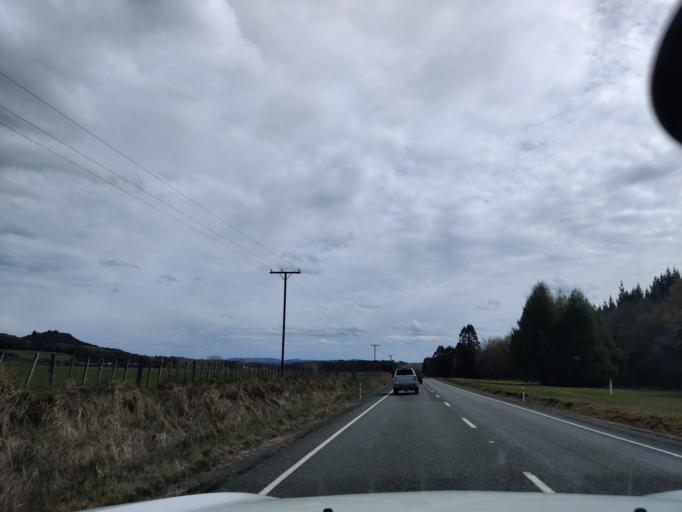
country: NZ
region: Manawatu-Wanganui
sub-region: Ruapehu District
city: Waiouru
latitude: -39.4735
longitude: 175.5418
